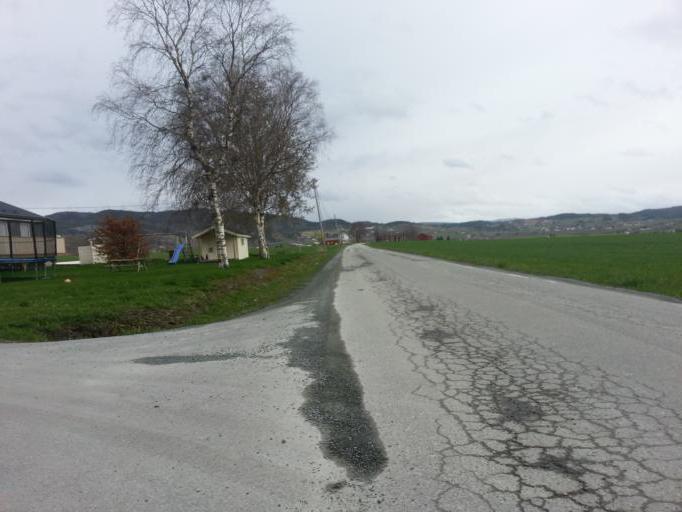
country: NO
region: Nord-Trondelag
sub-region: Levanger
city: Skogn
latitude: 63.6949
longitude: 11.2004
